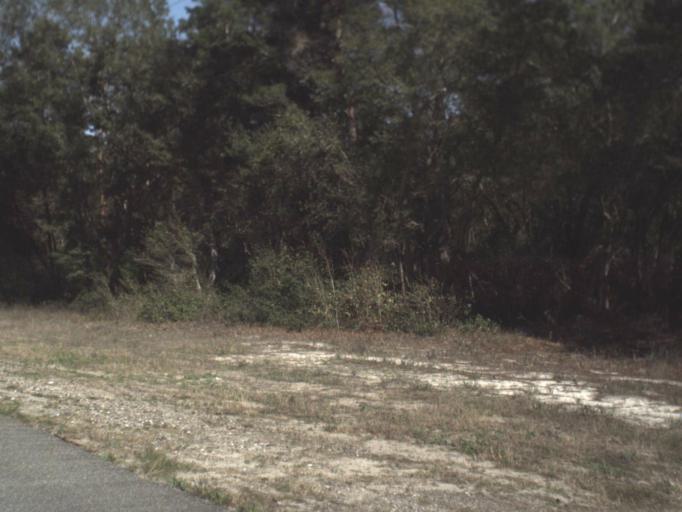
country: US
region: Florida
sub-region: Wakulla County
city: Crawfordville
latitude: 29.9291
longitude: -84.3986
